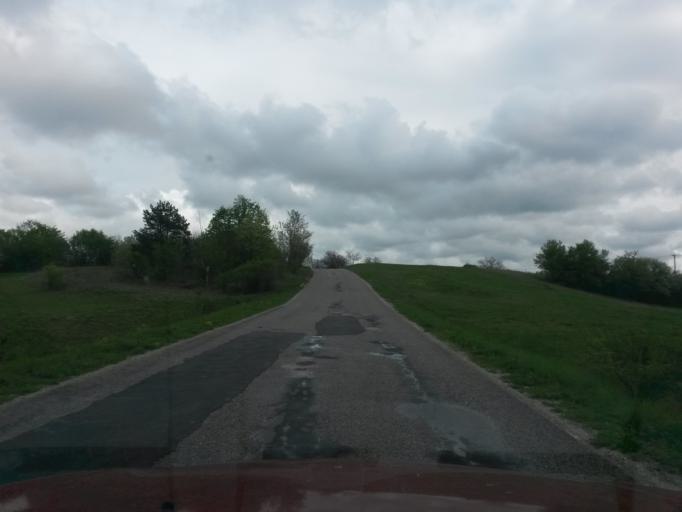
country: SK
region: Kosicky
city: Roznava
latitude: 48.5587
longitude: 20.5001
